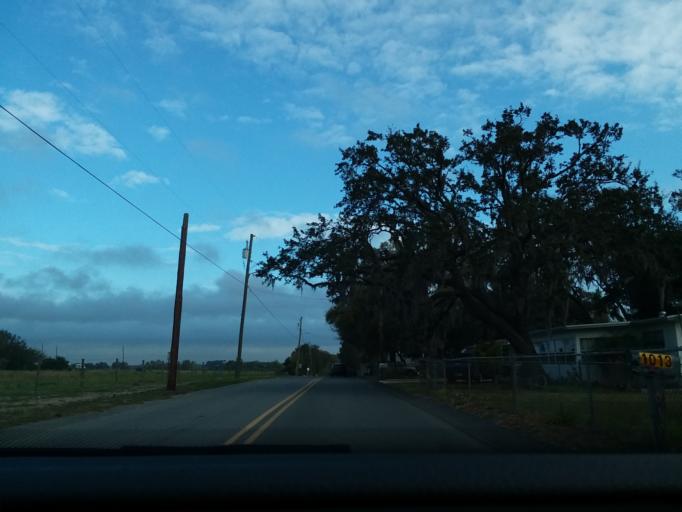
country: US
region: Florida
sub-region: Polk County
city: Haines City
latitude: 28.1226
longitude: -81.6526
